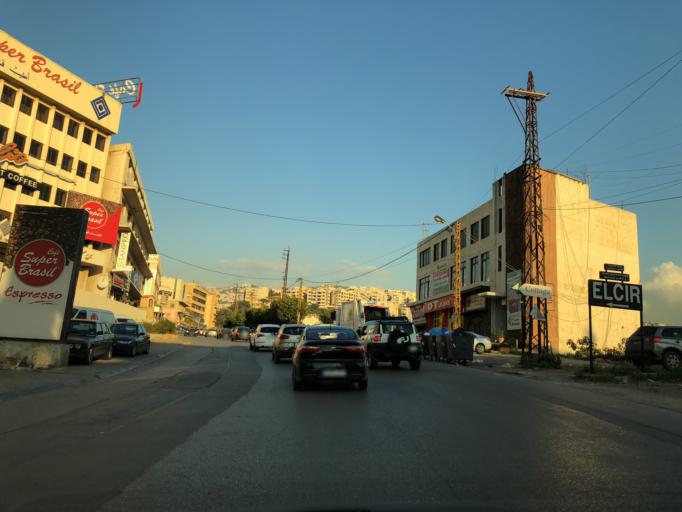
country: LB
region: Mont-Liban
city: Baabda
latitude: 33.8599
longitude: 35.5536
